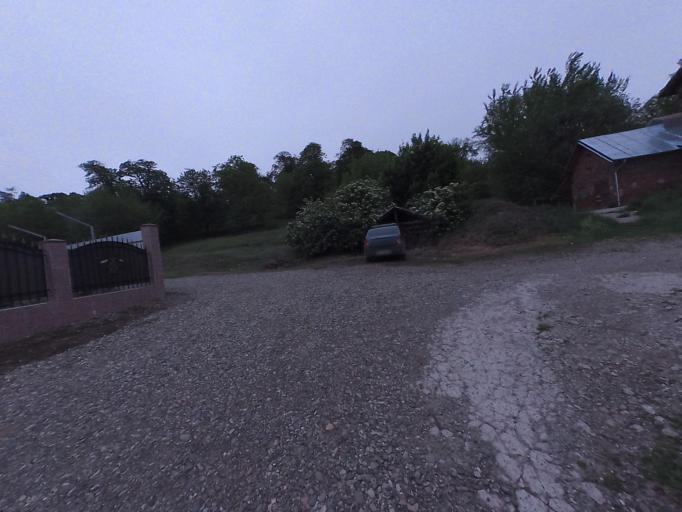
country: RO
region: Neamt
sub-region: Comuna Dulcesti
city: Dulcesti
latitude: 46.9665
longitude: 26.7864
